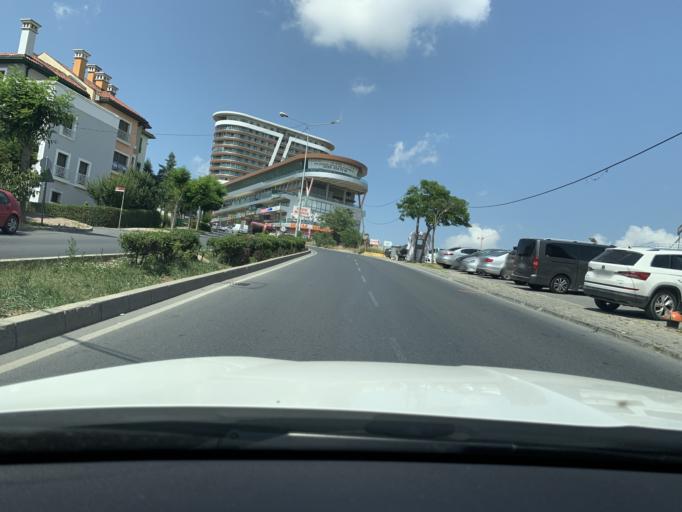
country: TR
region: Istanbul
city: Esenyurt
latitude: 41.0653
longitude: 28.7000
